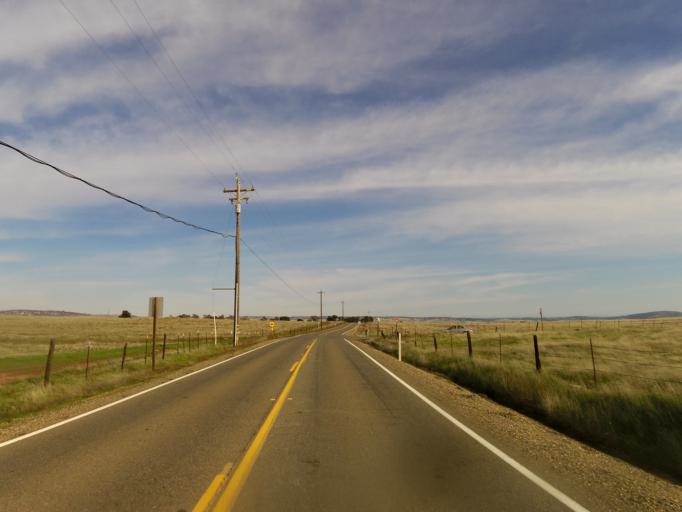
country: US
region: California
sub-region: Sacramento County
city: Folsom
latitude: 38.6171
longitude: -121.1425
